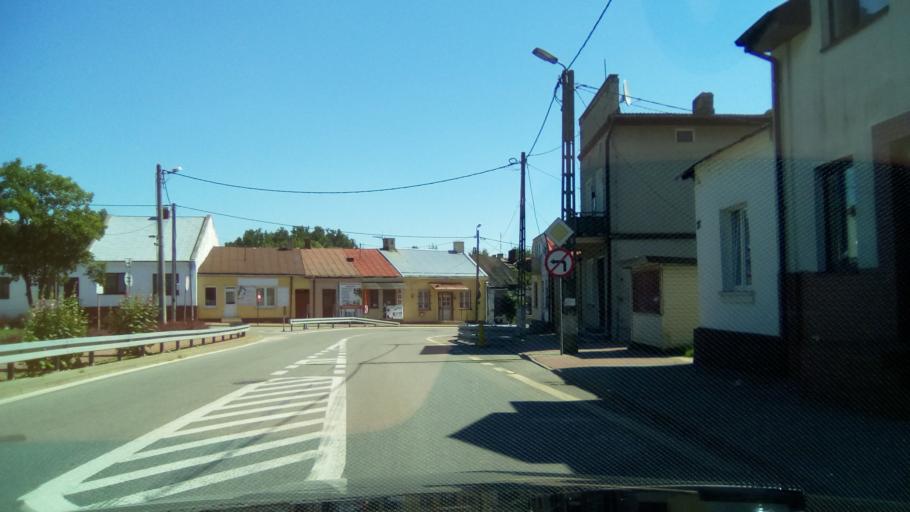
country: PL
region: Masovian Voivodeship
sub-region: Powiat przysuski
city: Odrzywol
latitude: 51.5193
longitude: 20.5563
